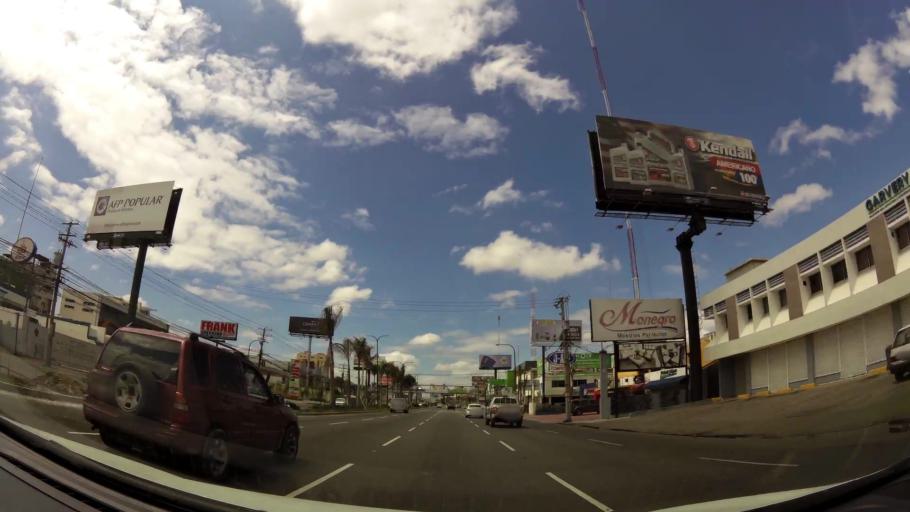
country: DO
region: Nacional
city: Bella Vista
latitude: 18.4590
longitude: -69.9440
